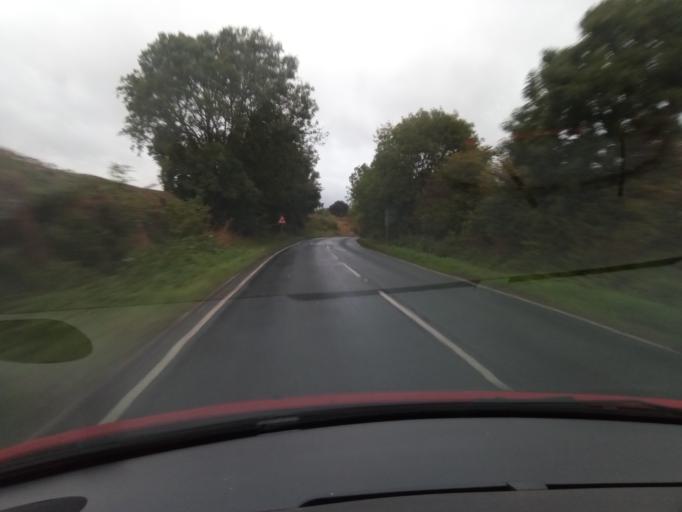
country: GB
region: England
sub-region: Darlington
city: High Coniscliffe
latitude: 54.4715
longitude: -1.6697
